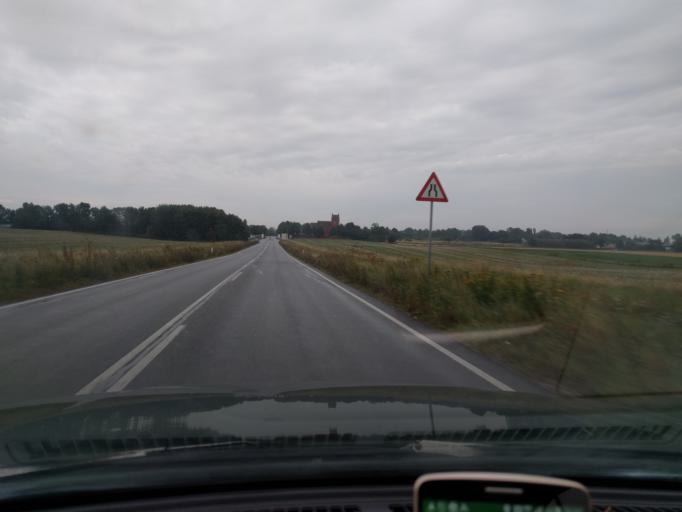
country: DK
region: Zealand
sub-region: Naestved Kommune
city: Naestved
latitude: 55.1617
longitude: 11.8177
